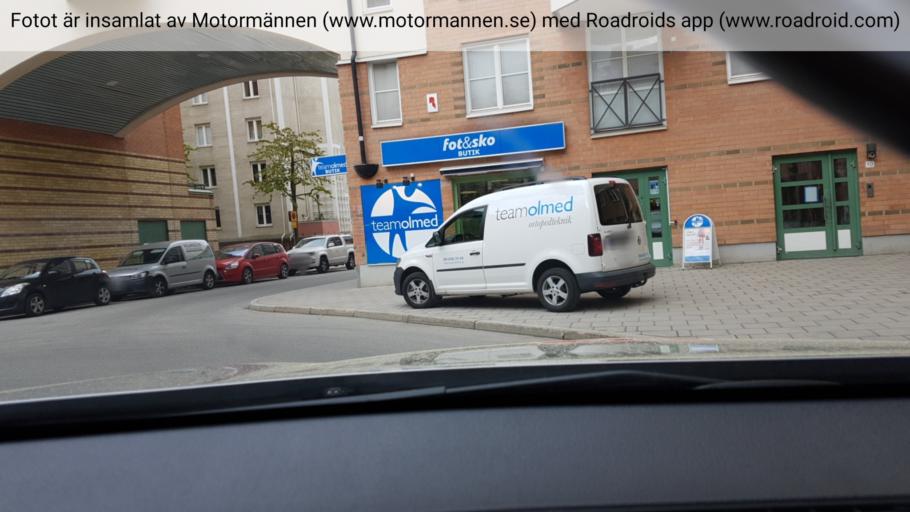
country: SE
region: Stockholm
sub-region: Stockholms Kommun
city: Arsta
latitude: 59.3128
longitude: 18.0582
